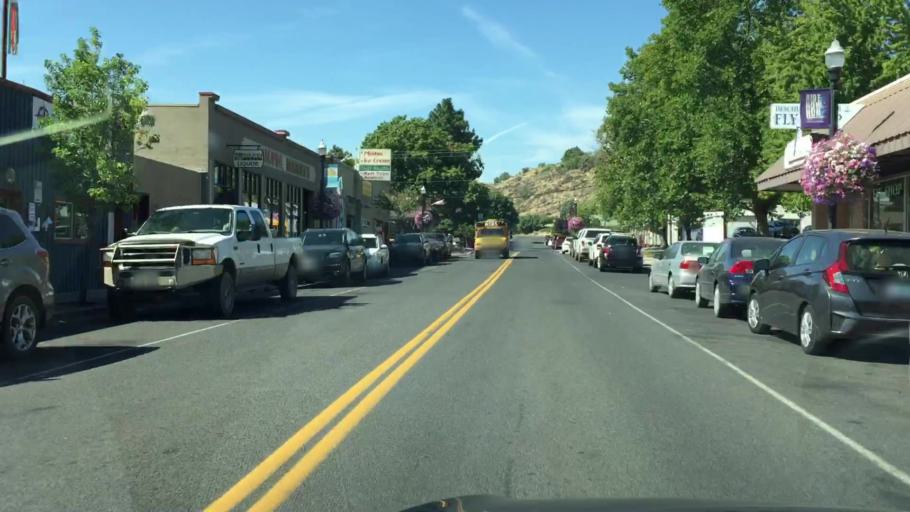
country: US
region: Oregon
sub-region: Wasco County
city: The Dalles
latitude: 45.1752
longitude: -121.0810
